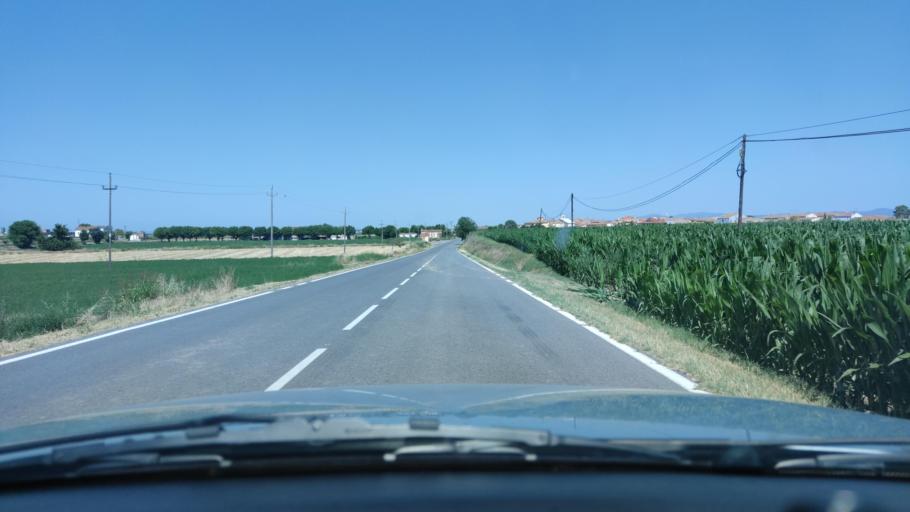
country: ES
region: Catalonia
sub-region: Provincia de Lleida
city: Linyola
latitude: 41.6939
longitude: 0.9564
